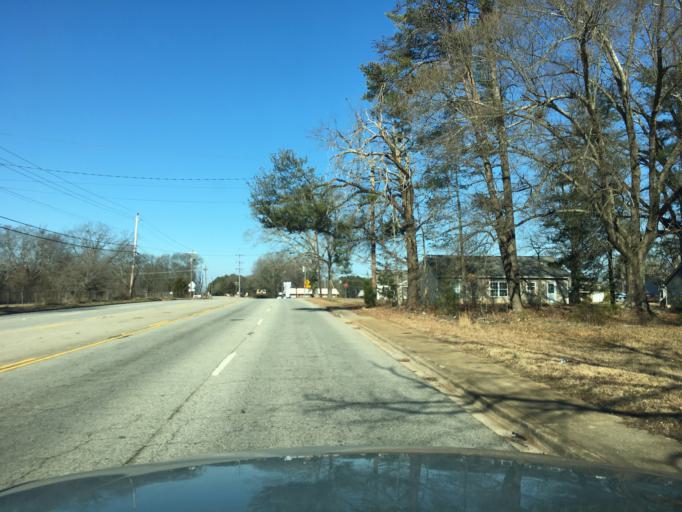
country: US
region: South Carolina
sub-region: Greenville County
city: Berea
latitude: 34.8854
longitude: -82.4593
